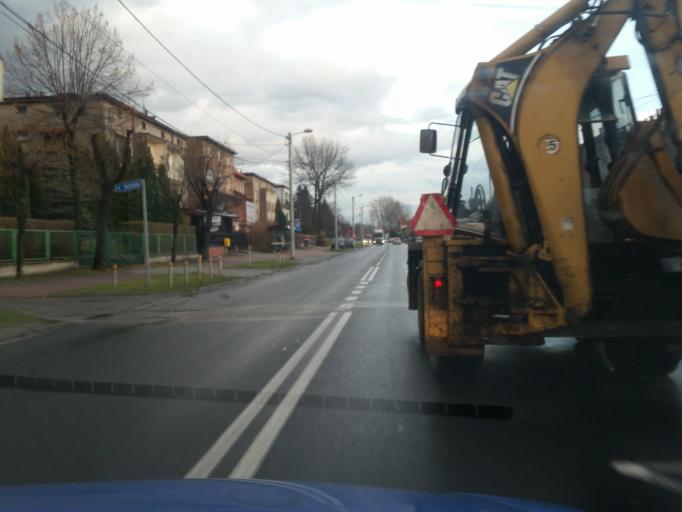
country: PL
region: Silesian Voivodeship
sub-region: Sosnowiec
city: Sosnowiec
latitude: 50.2716
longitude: 19.1567
